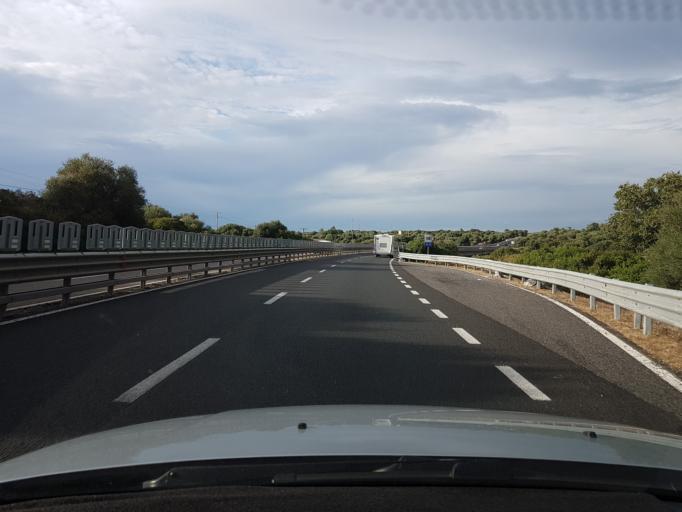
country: IT
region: Sardinia
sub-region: Provincia di Oristano
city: Paulilatino
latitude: 40.0819
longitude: 8.7519
